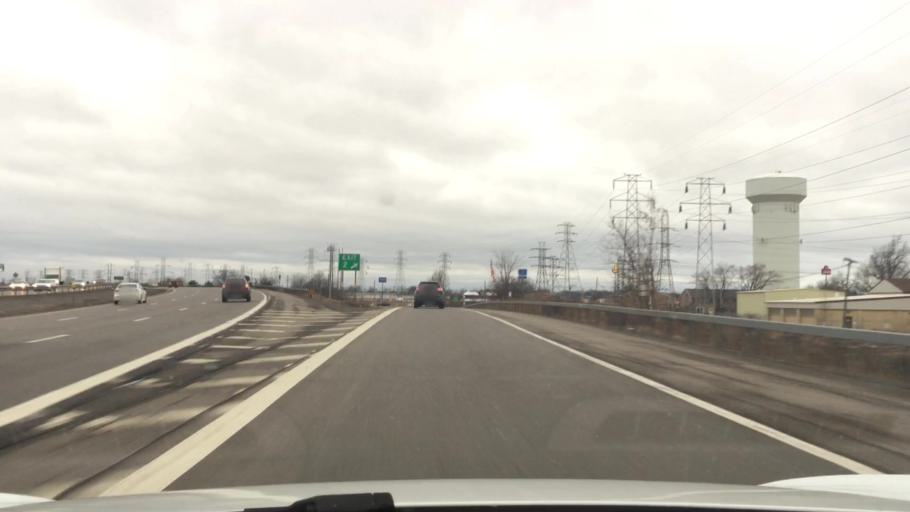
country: US
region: New York
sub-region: Erie County
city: Tonawanda
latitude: 43.0011
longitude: -78.8492
